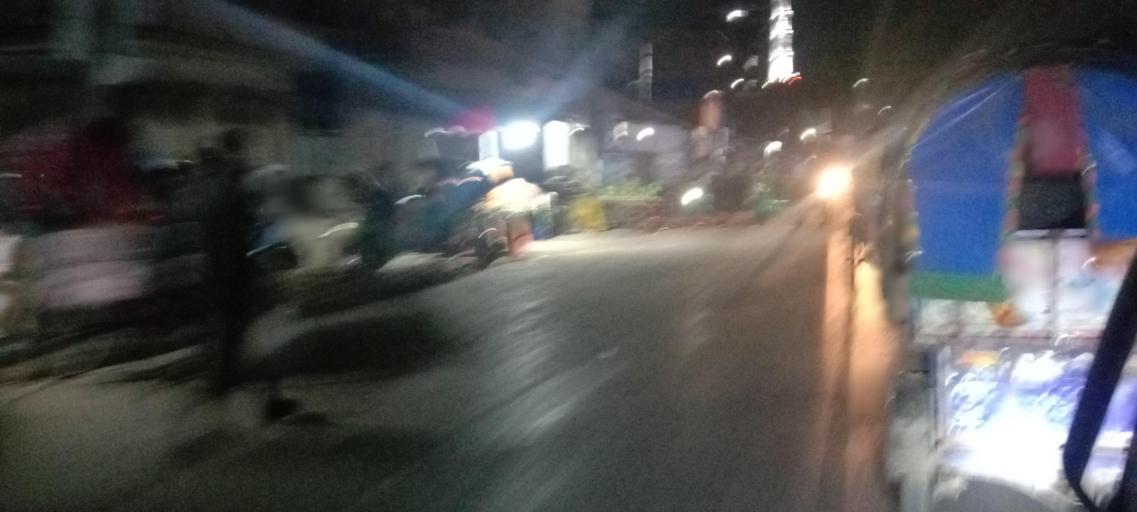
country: BD
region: Dhaka
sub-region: Dhaka
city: Dhaka
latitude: 23.7014
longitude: 90.3923
